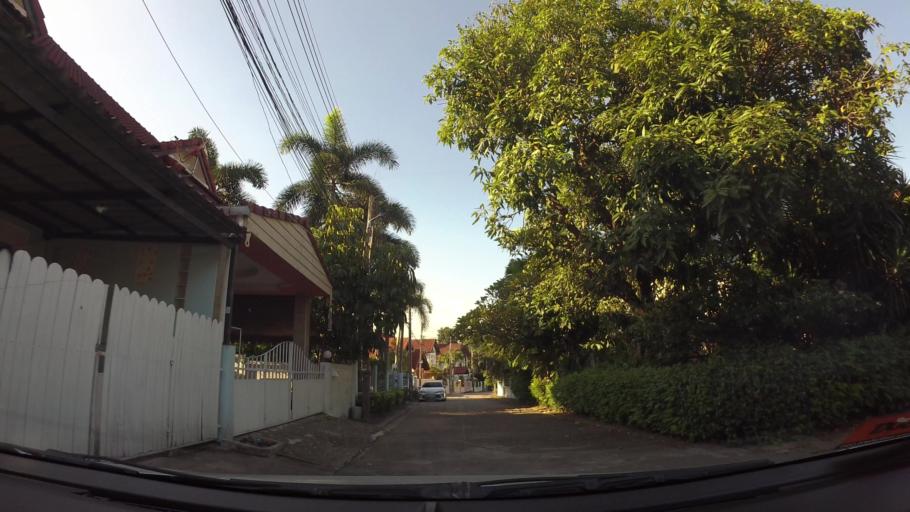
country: TH
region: Chon Buri
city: Si Racha
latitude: 13.1466
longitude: 100.9300
